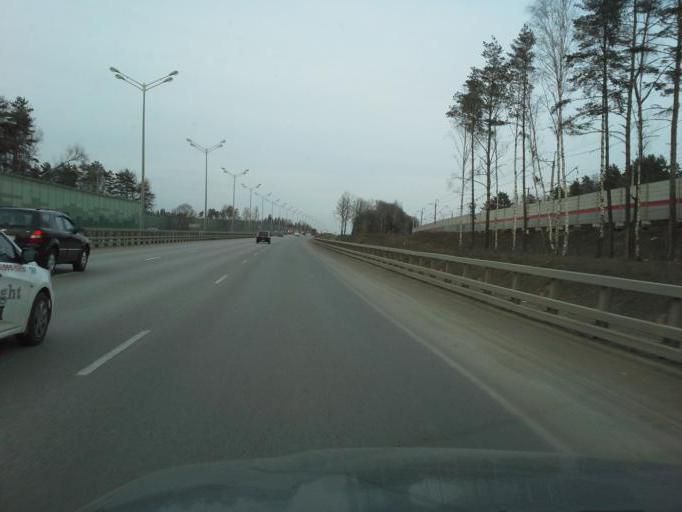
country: RU
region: Moskovskaya
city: Lesnoy Gorodok
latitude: 55.6416
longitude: 37.2341
